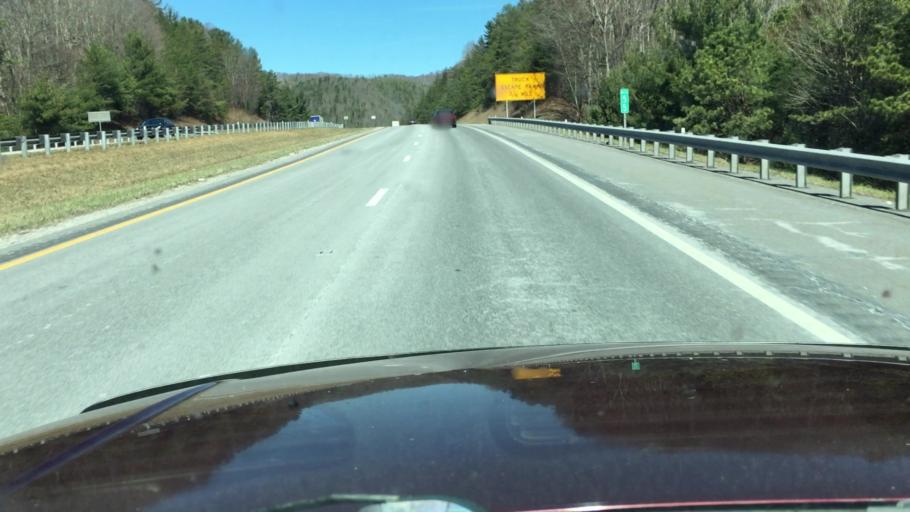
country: US
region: Virginia
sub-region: Bland County
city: Bland
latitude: 37.1305
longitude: -81.1203
